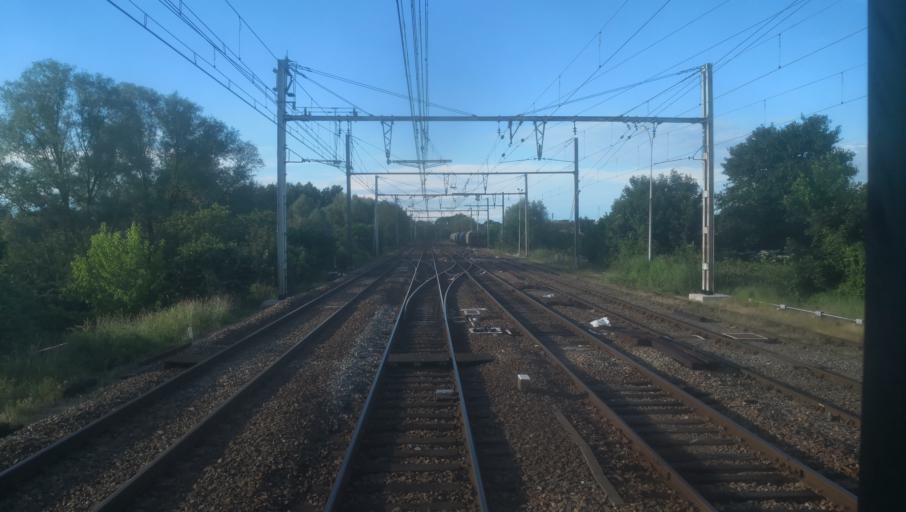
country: FR
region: Centre
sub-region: Departement de l'Indre
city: Issoudun
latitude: 46.9514
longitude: 1.9872
